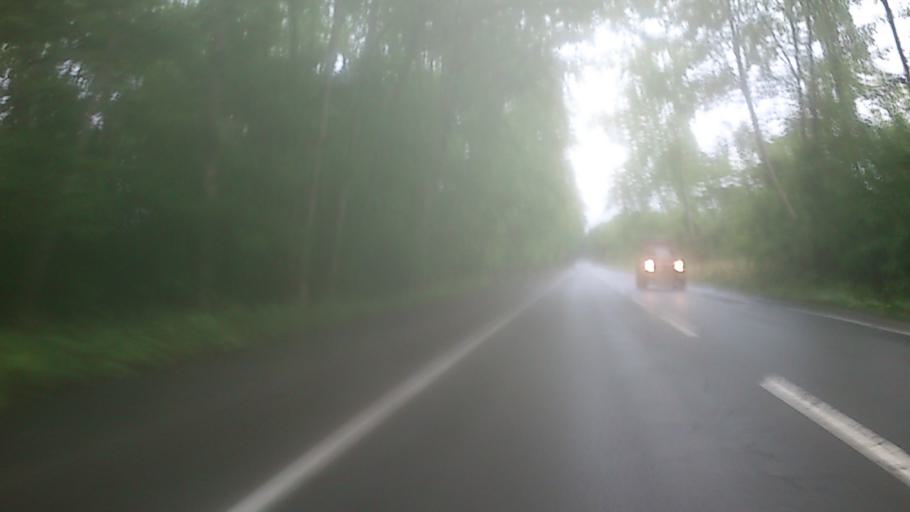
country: JP
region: Hokkaido
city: Tomakomai
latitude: 42.7644
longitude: 141.4193
